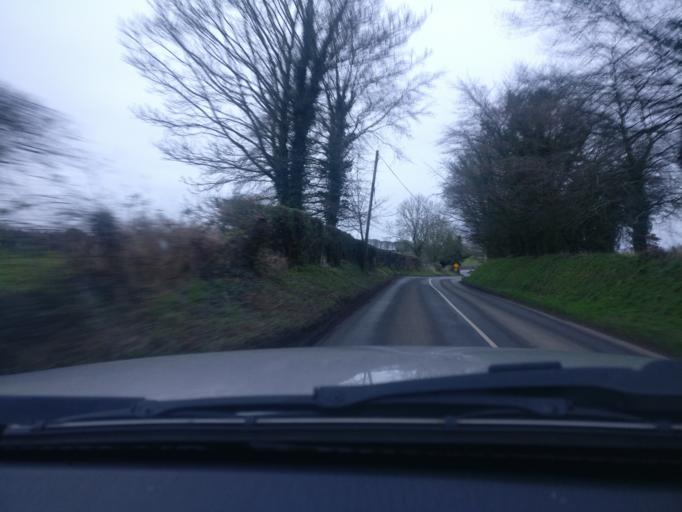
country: IE
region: Leinster
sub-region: An Mhi
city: Dunshaughlin
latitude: 53.4876
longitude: -6.6088
